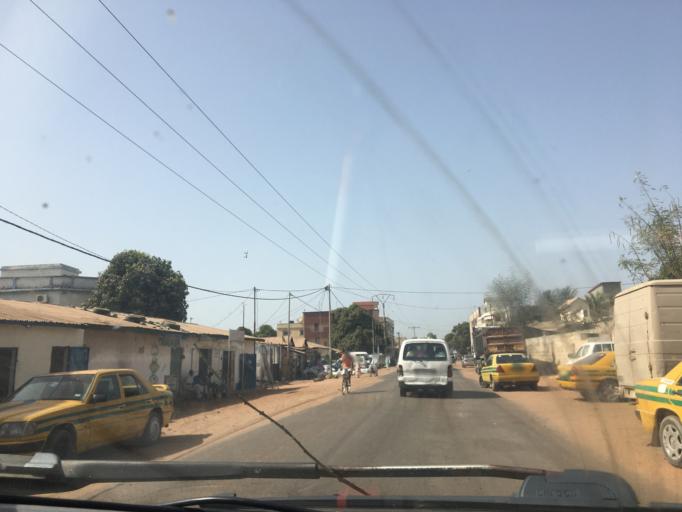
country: GM
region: Western
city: Abuko
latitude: 13.3931
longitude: -16.6743
